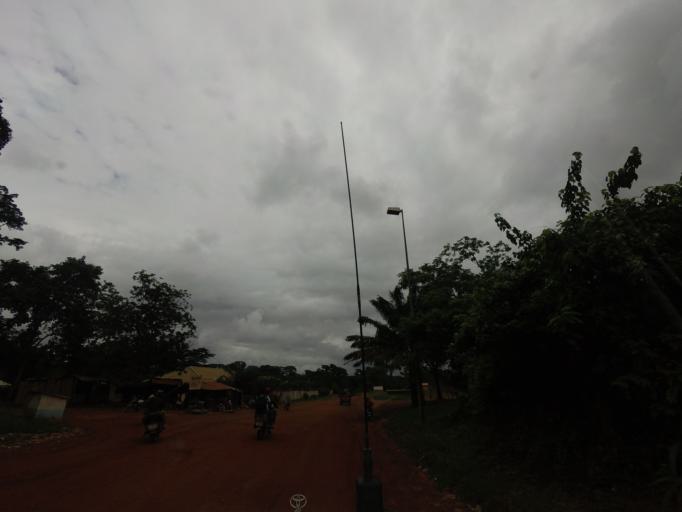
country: LR
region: Nimba
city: Sanniquellie
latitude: 7.3383
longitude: -8.9663
